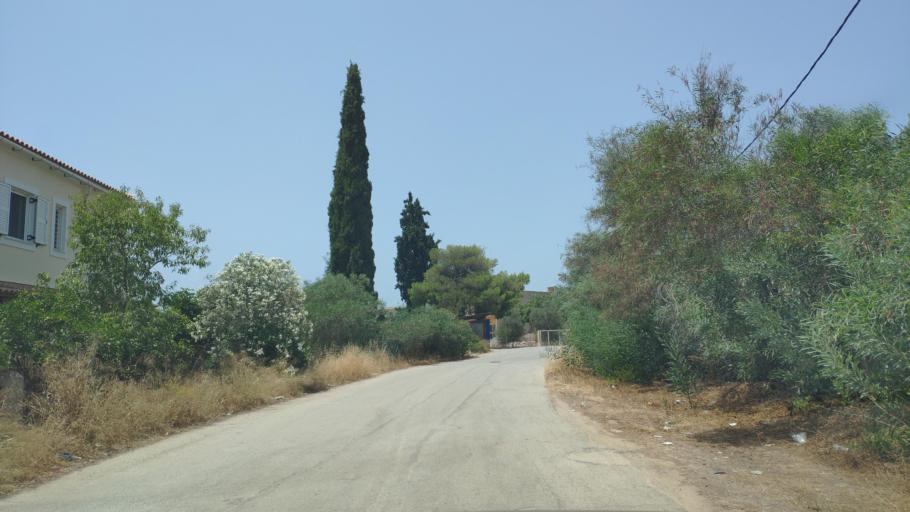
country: GR
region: Peloponnese
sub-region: Nomos Argolidos
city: Porto Cheli
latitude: 37.3303
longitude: 23.1475
